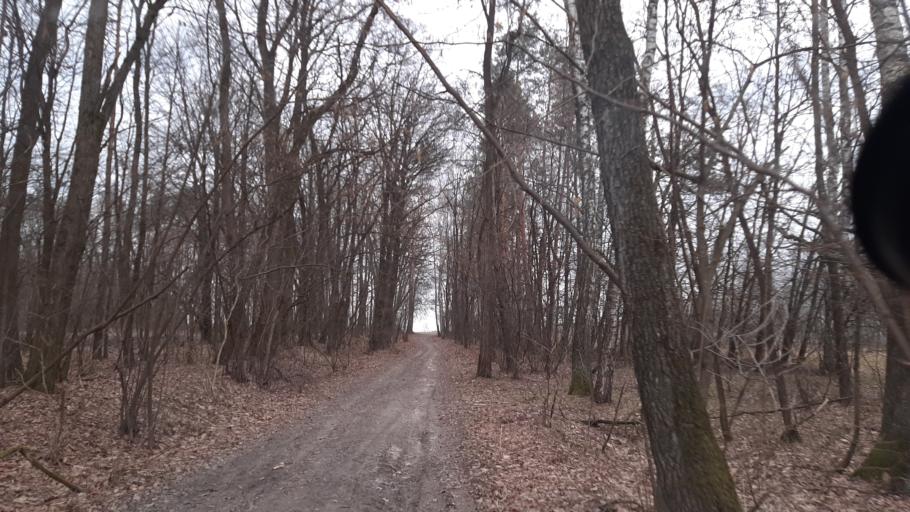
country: PL
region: Lublin Voivodeship
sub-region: Powiat lubelski
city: Garbow
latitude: 51.4022
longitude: 22.3890
